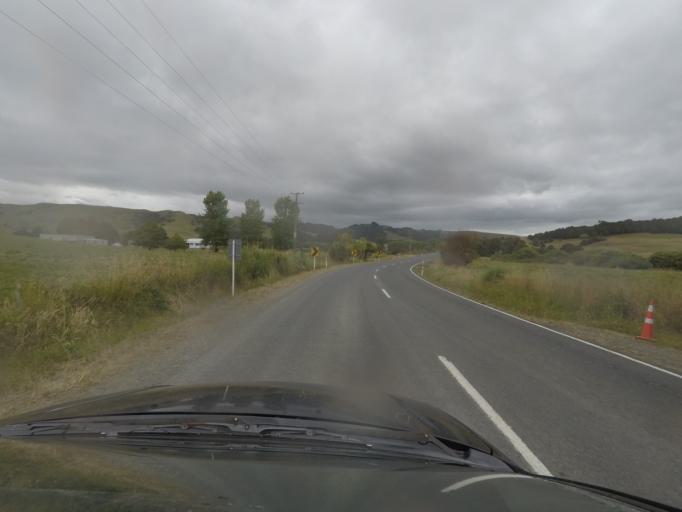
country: NZ
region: Auckland
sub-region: Auckland
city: Warkworth
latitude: -36.2812
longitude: 174.6692
